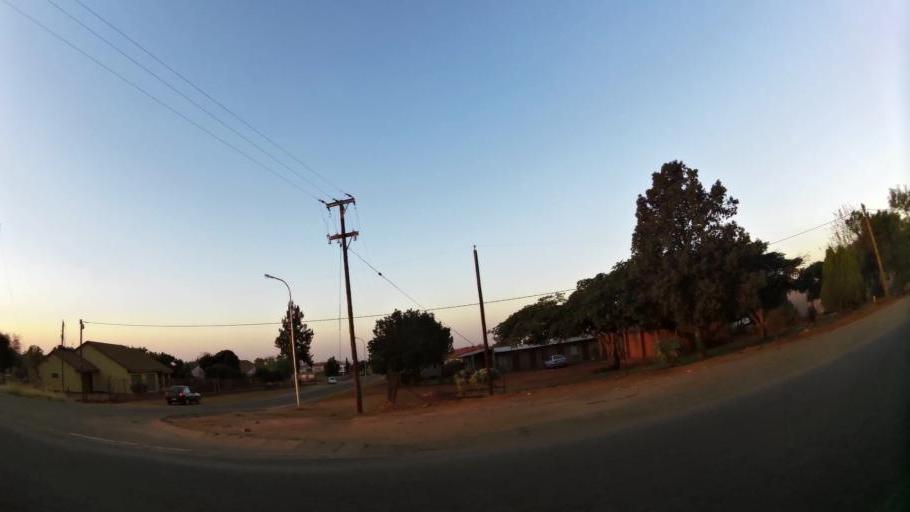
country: ZA
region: North-West
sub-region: Bojanala Platinum District Municipality
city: Rustenburg
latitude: -25.6093
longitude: 27.1884
